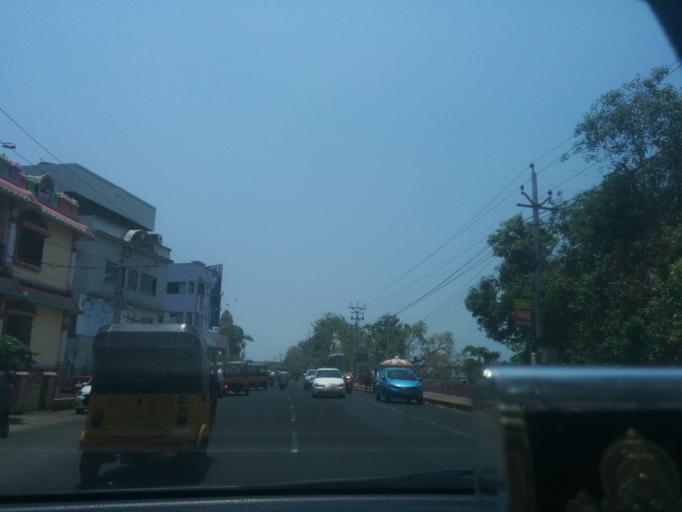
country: IN
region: Andhra Pradesh
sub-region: East Godavari
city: Rajahmundry
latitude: 17.0040
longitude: 81.7670
